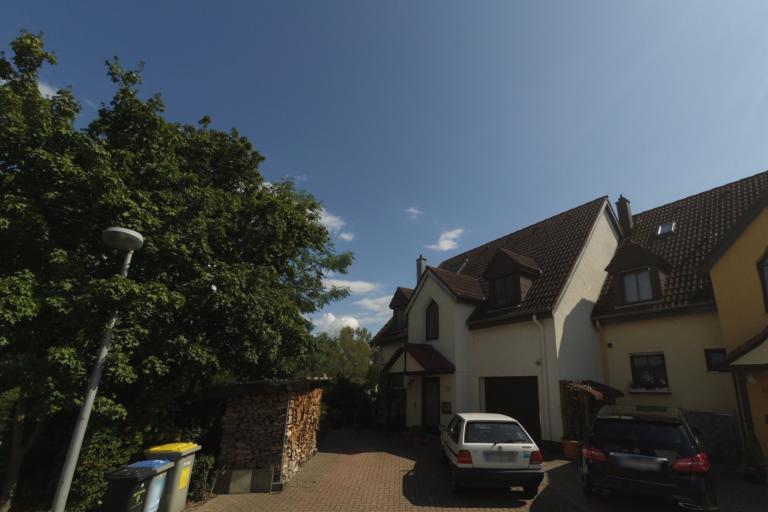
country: DE
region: Baden-Wuerttemberg
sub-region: Karlsruhe Region
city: Bruhl
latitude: 49.4150
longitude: 8.5330
